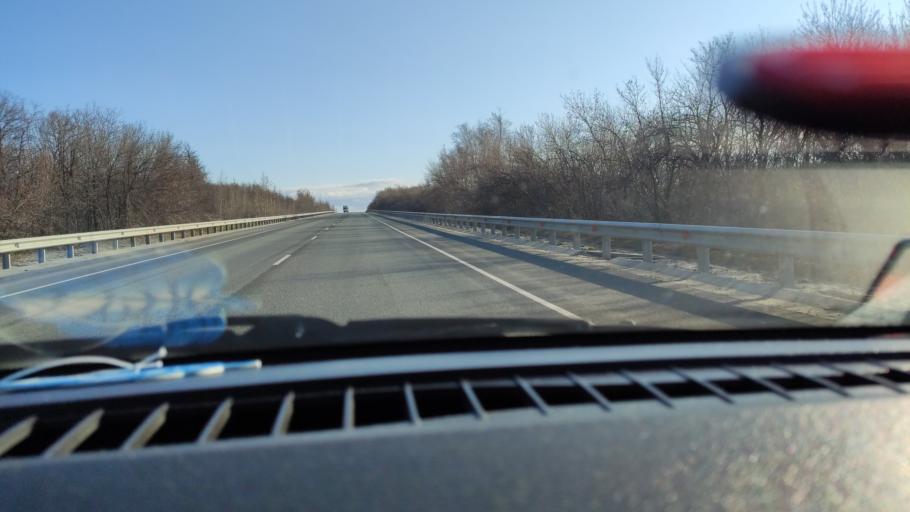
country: RU
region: Saratov
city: Dukhovnitskoye
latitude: 52.6197
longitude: 48.1710
